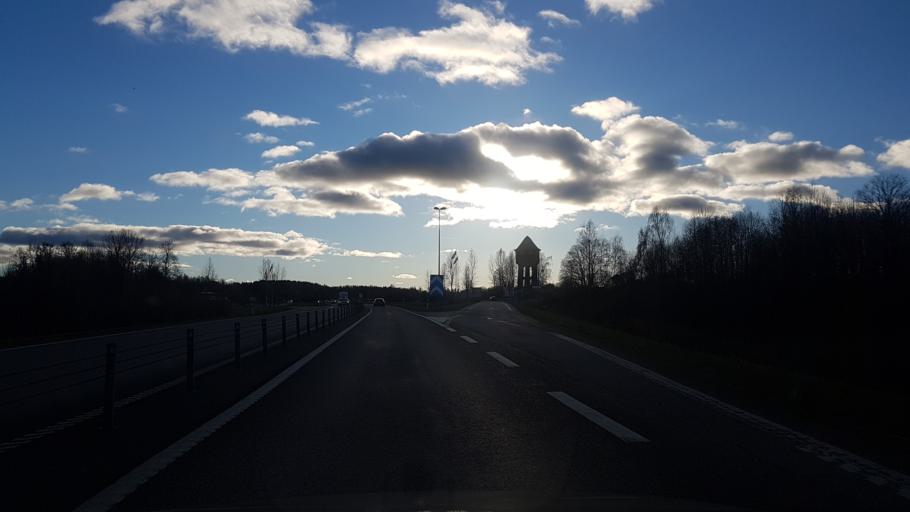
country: SE
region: Gaevleborg
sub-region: Sandvikens Kommun
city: Jarbo
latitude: 60.5837
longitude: 16.5410
